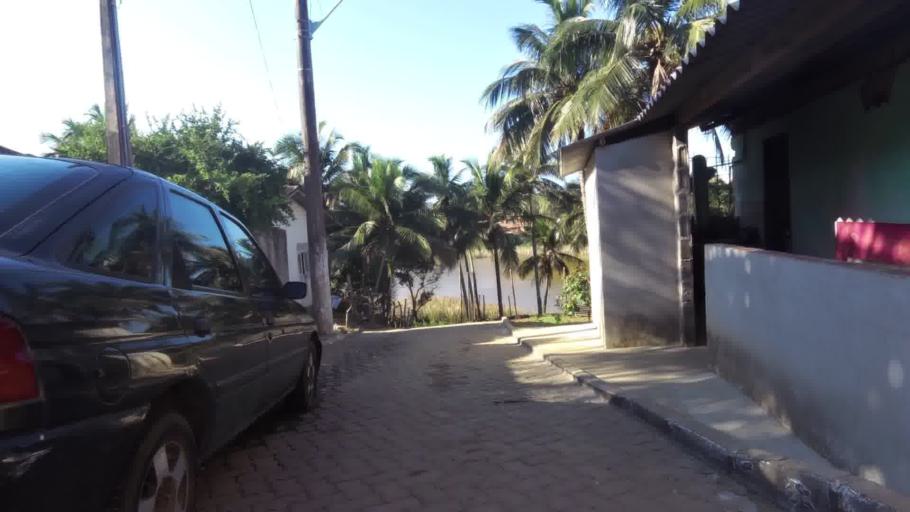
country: BR
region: Espirito Santo
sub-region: Guarapari
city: Guarapari
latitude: -20.7486
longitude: -40.5613
